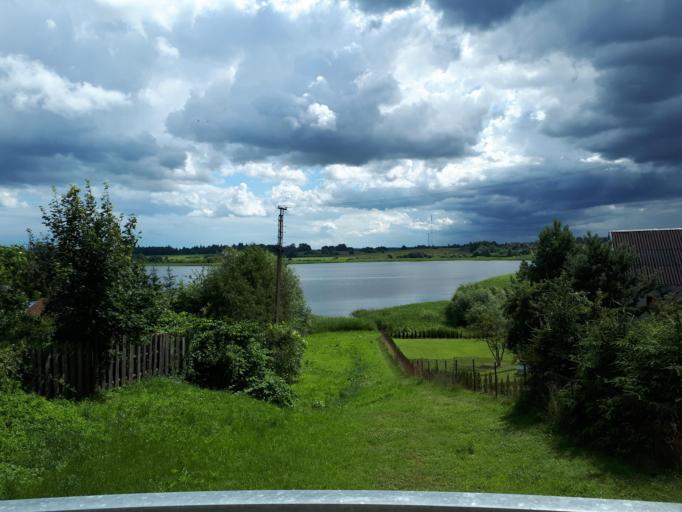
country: LT
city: Jieznas
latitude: 54.5980
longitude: 24.1725
